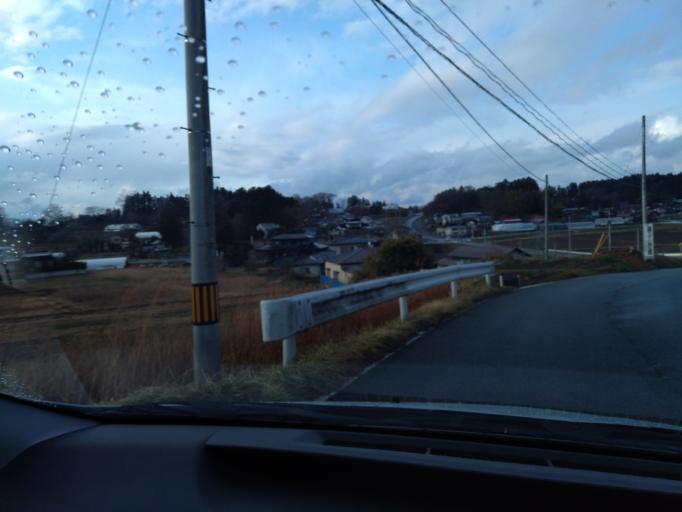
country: JP
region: Iwate
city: Ichinoseki
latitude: 38.7404
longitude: 141.1208
